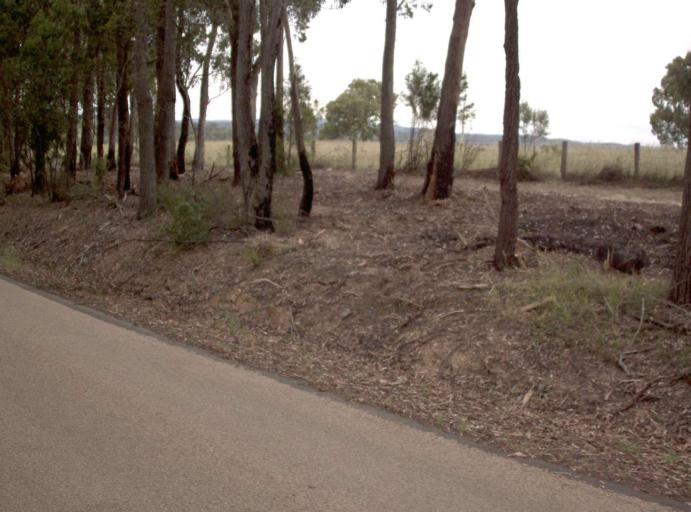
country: AU
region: Victoria
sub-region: East Gippsland
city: Bairnsdale
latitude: -37.7325
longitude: 147.5924
